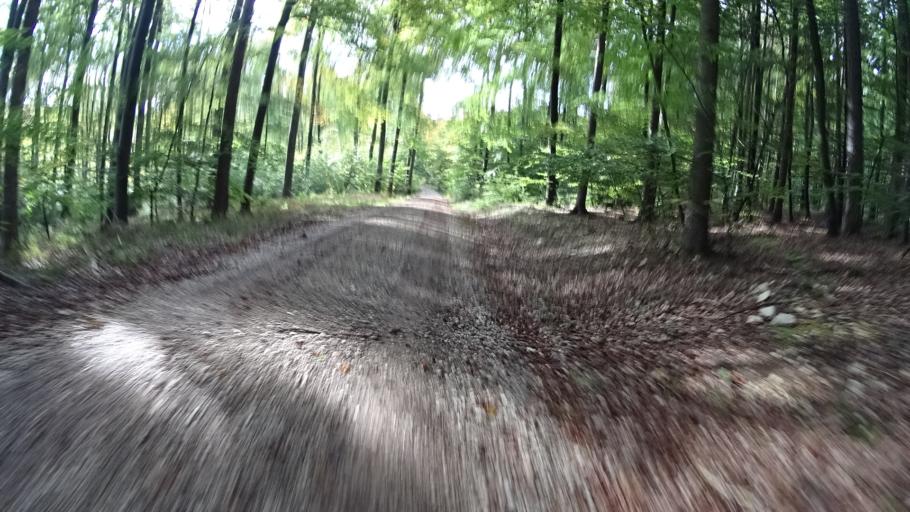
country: DE
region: Bavaria
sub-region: Upper Bavaria
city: Walting
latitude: 48.9054
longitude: 11.3103
